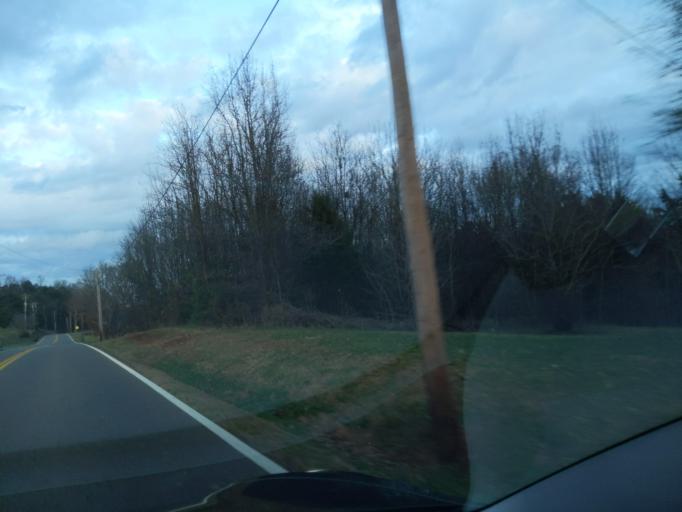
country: US
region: Tennessee
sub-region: Jefferson County
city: Dandridge
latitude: 36.0056
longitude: -83.4336
